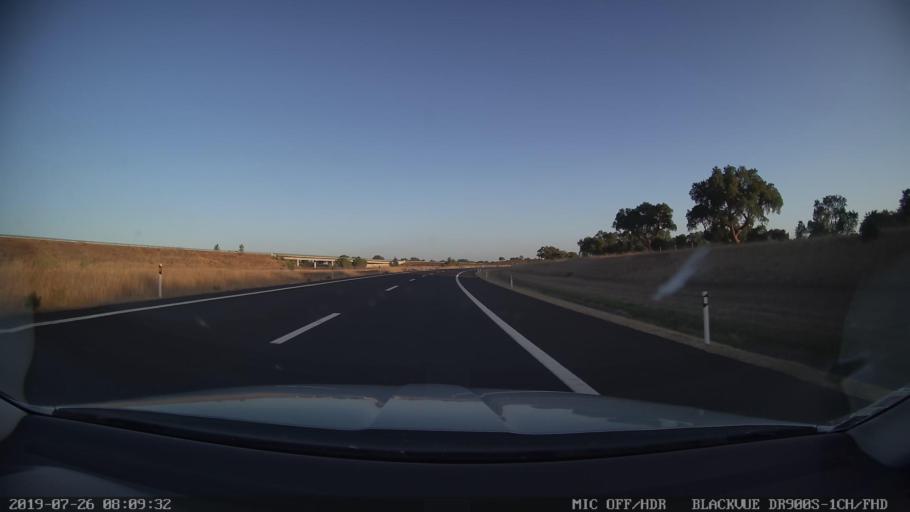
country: PT
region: Santarem
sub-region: Benavente
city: Poceirao
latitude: 38.9052
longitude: -8.7841
